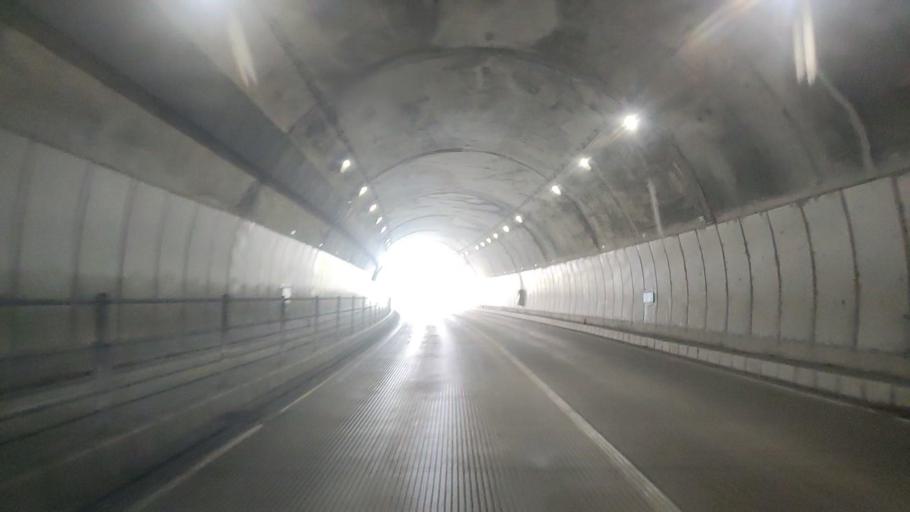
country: JP
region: Gifu
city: Tarui
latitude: 35.3727
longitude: 136.4563
